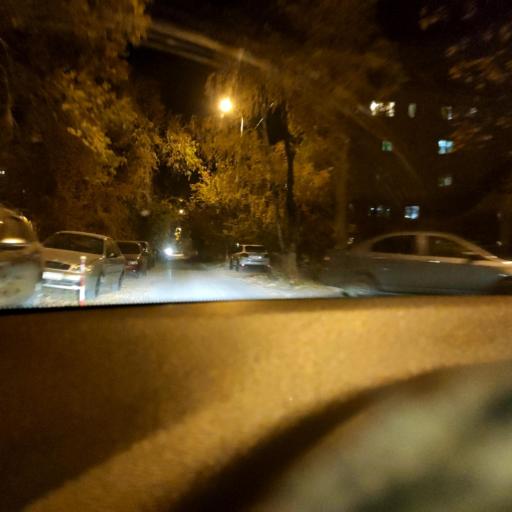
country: RU
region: Samara
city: Samara
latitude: 53.2179
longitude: 50.2311
